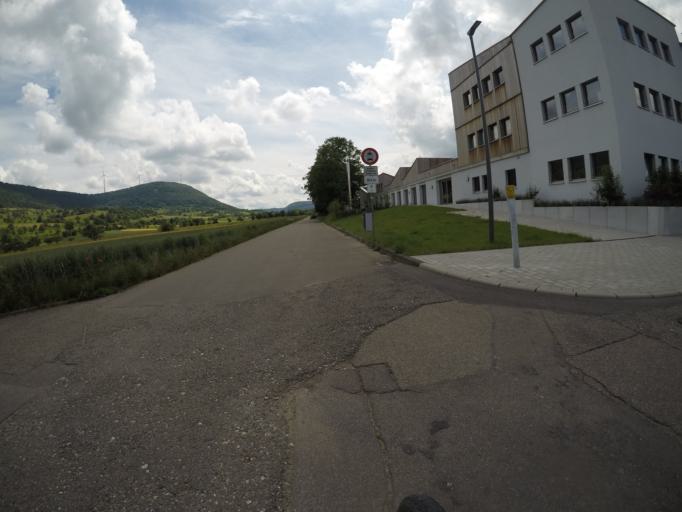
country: DE
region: Baden-Wuerttemberg
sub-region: Regierungsbezirk Stuttgart
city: Gingen an der Fils
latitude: 48.6540
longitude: 9.7882
